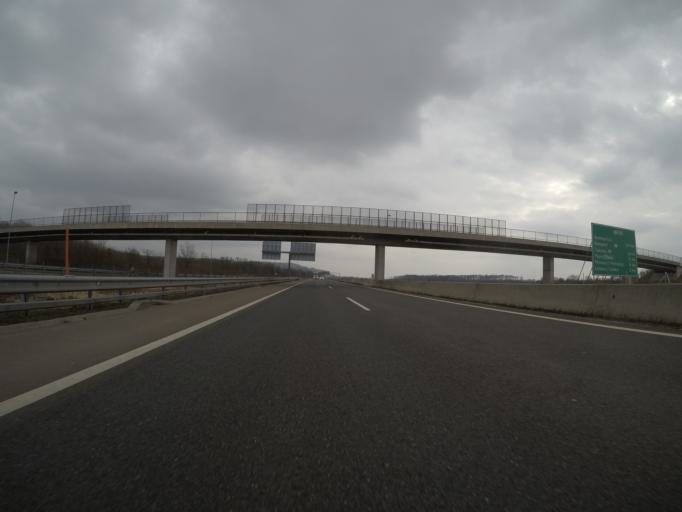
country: SI
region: Lendava-Lendva
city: Lendava
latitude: 46.5855
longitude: 16.4311
